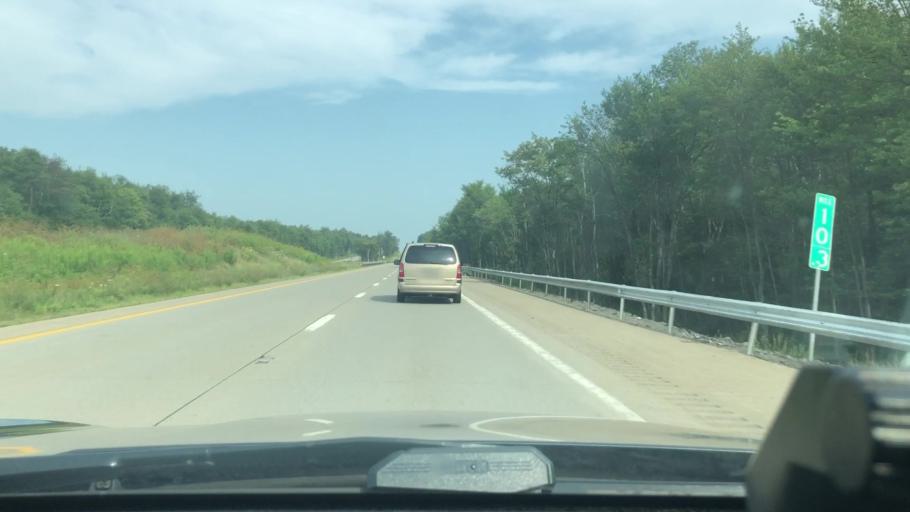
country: US
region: Pennsylvania
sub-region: Monroe County
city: Pocono Pines
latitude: 41.2039
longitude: -75.4598
